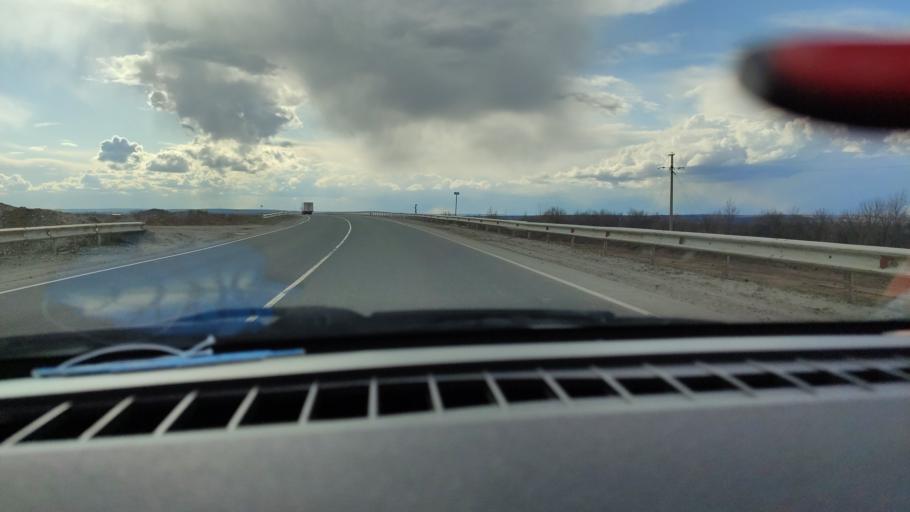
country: RU
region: Saratov
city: Sennoy
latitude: 52.1598
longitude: 47.0430
